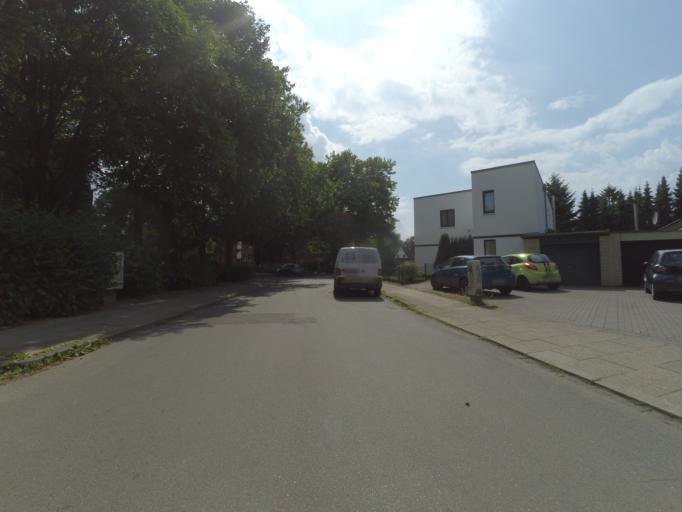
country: DE
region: Hamburg
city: Eidelstedt
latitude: 53.5759
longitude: 9.8678
